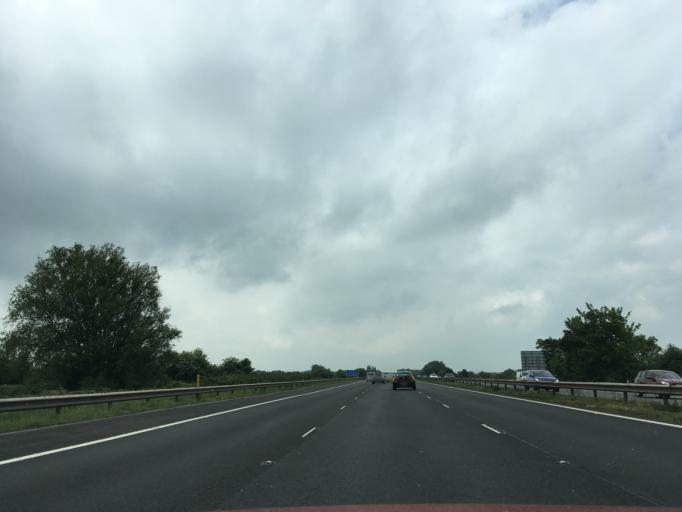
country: GB
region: England
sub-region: Somerset
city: Highbridge
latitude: 51.2280
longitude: -2.9524
